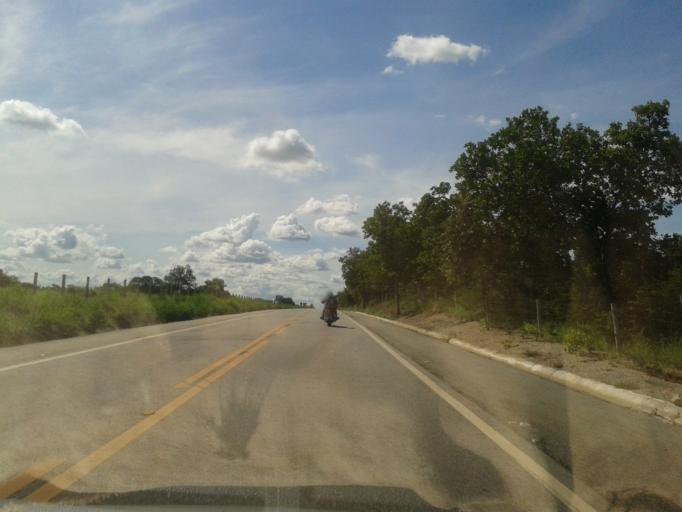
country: BR
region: Goias
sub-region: Itapirapua
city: Itapirapua
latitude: -15.2992
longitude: -50.4549
